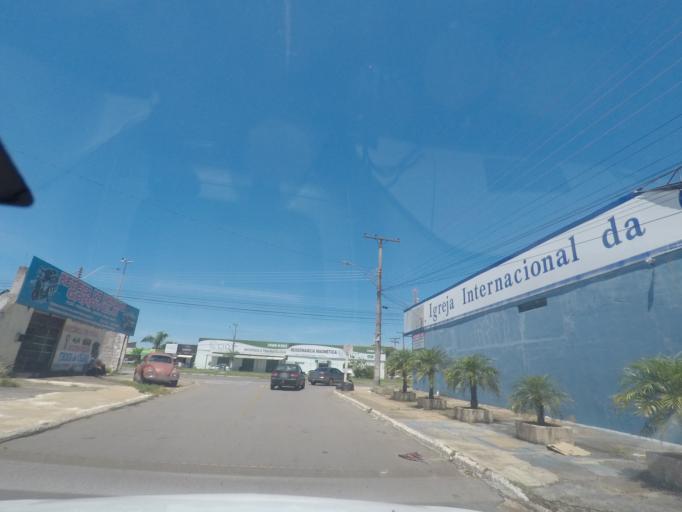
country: BR
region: Goias
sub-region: Aparecida De Goiania
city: Aparecida de Goiania
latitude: -16.7692
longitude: -49.3436
